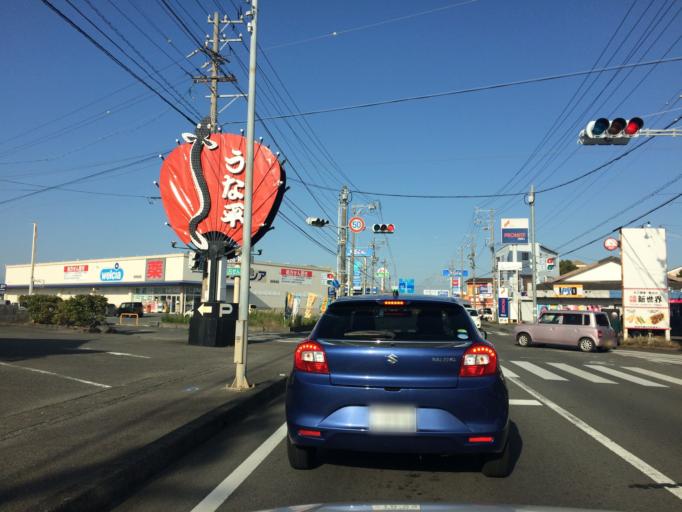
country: JP
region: Shizuoka
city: Shimada
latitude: 34.7648
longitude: 138.2484
